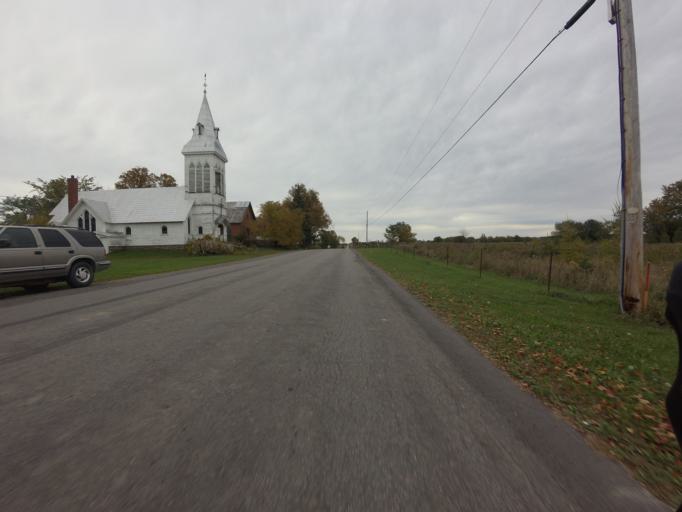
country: CA
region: Ontario
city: Bells Corners
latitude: 45.0922
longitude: -75.7560
